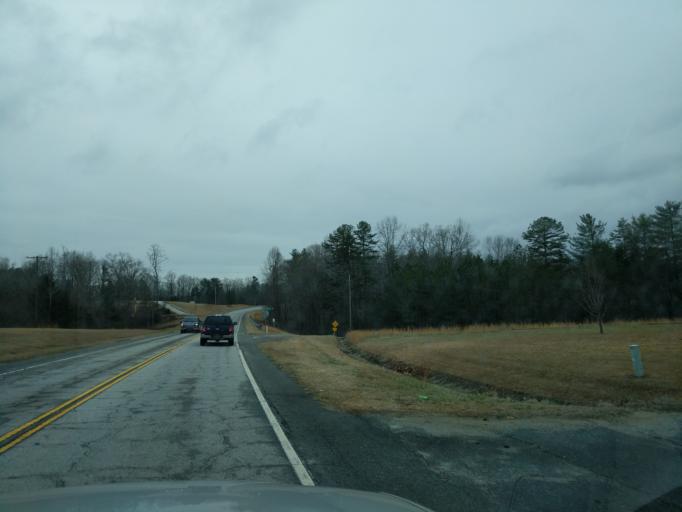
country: US
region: South Carolina
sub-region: Oconee County
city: Walhalla
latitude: 34.8491
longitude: -83.0328
